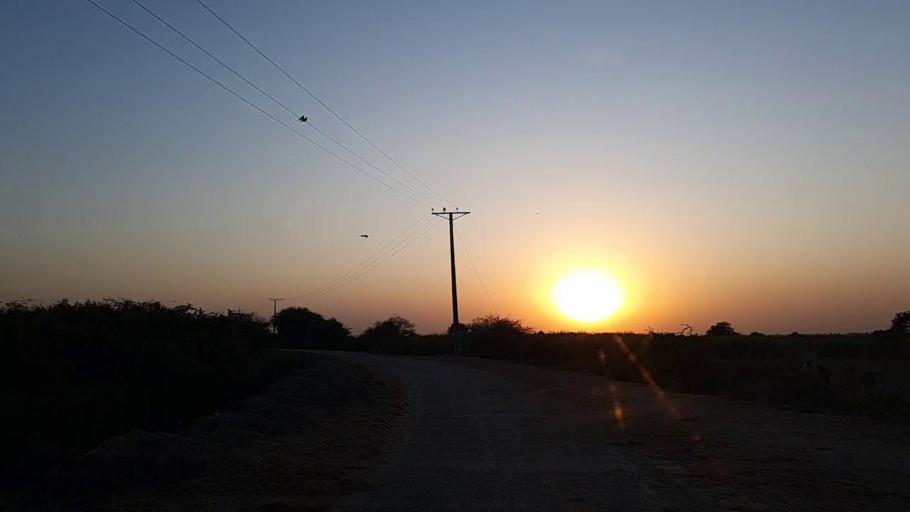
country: PK
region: Sindh
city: Mirpur Batoro
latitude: 24.6320
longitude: 68.1868
